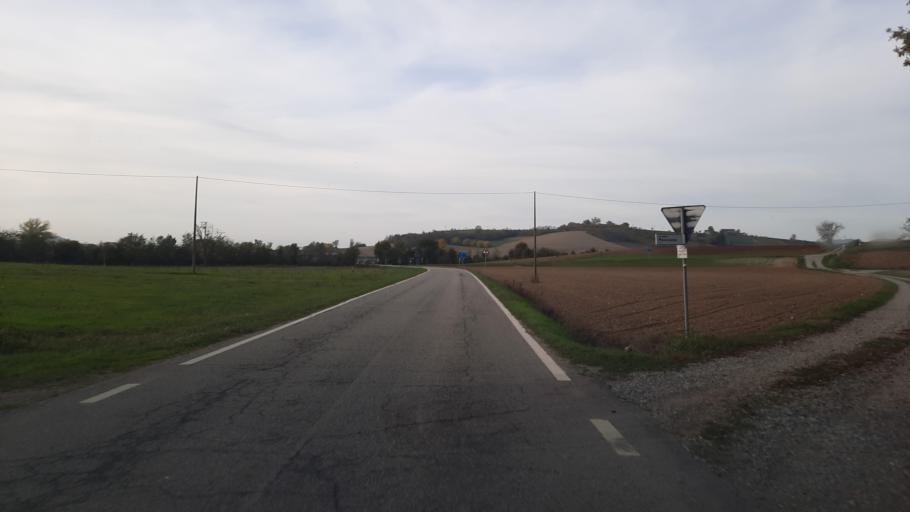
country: IT
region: Piedmont
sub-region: Provincia di Asti
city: Castell'Alfero
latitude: 45.0017
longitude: 8.2180
